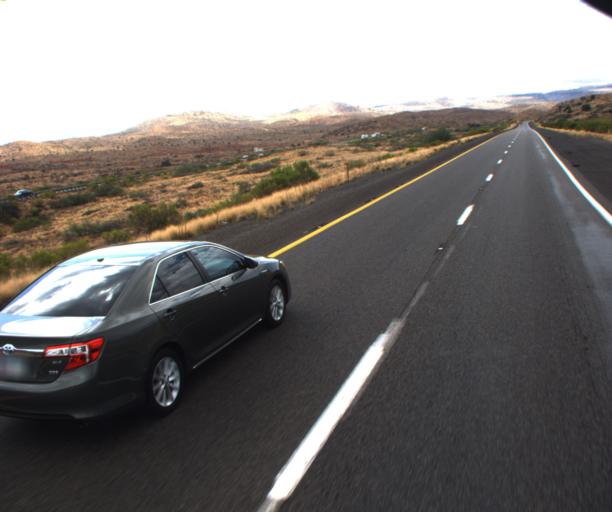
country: US
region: Arizona
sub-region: Yavapai County
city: Cordes Lakes
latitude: 34.2792
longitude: -112.1180
